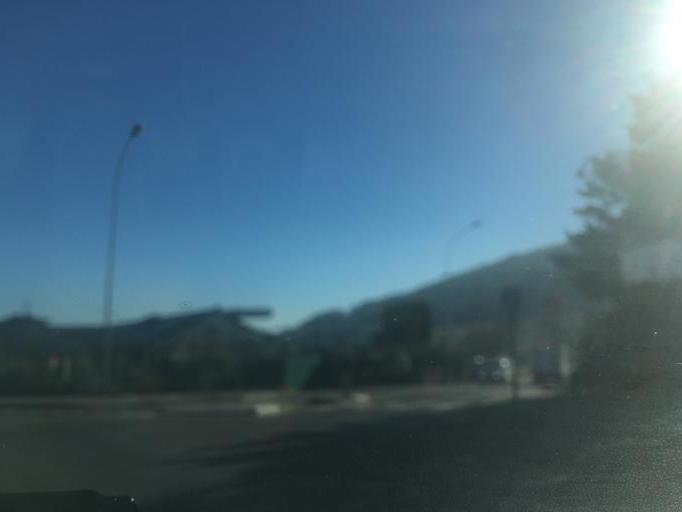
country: FR
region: Provence-Alpes-Cote d'Azur
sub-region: Departement du Var
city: Draguignan
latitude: 43.5264
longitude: 6.4552
